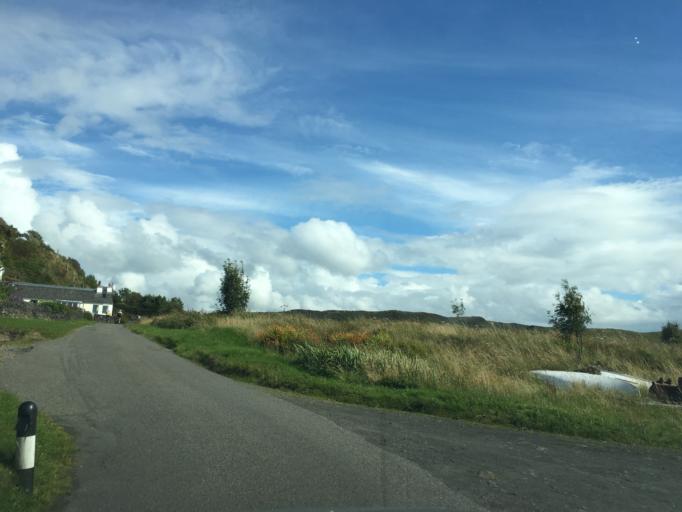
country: GB
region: Scotland
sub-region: Argyll and Bute
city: Isle Of Mull
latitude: 56.2496
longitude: -5.6535
